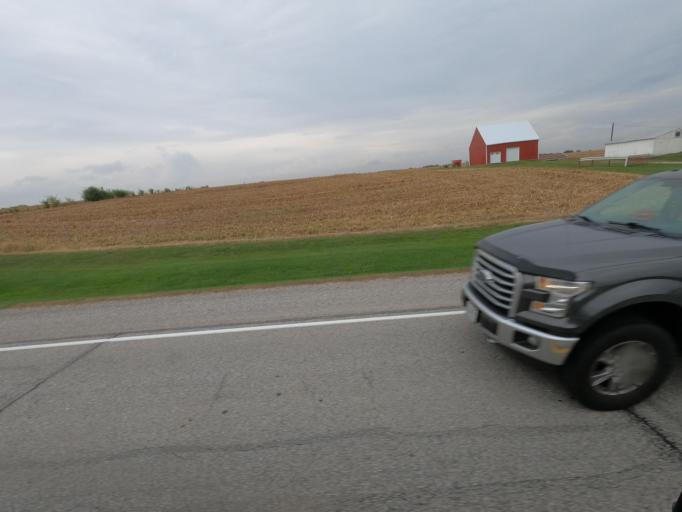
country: US
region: Iowa
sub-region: Van Buren County
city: Keosauqua
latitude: 40.8567
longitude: -92.0729
